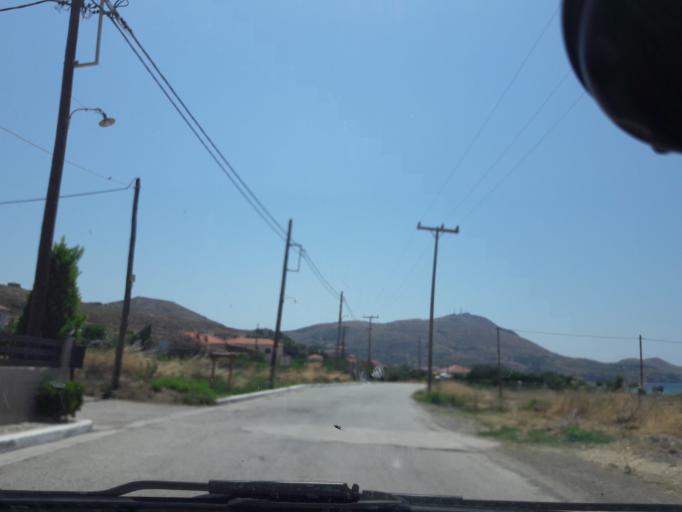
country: GR
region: North Aegean
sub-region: Nomos Lesvou
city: Myrina
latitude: 39.9311
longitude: 25.0641
